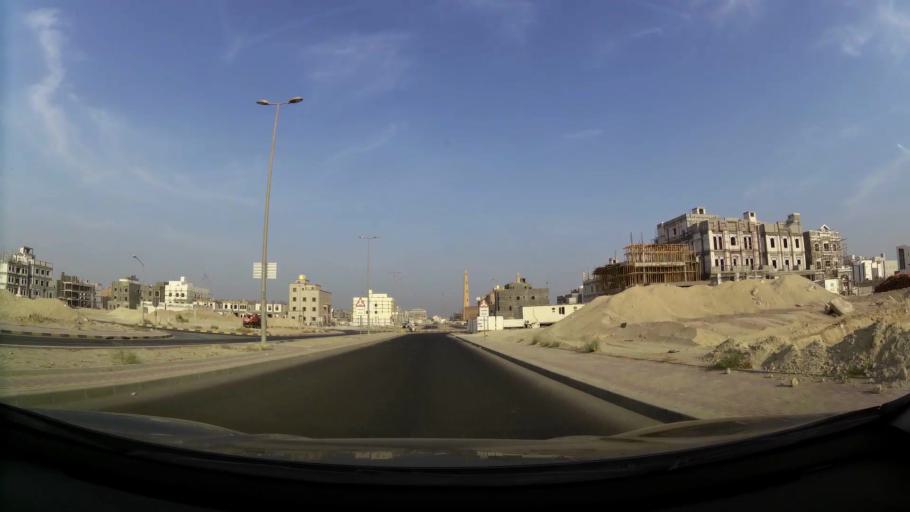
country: KW
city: Al Funaytis
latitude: 29.2194
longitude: 48.0897
